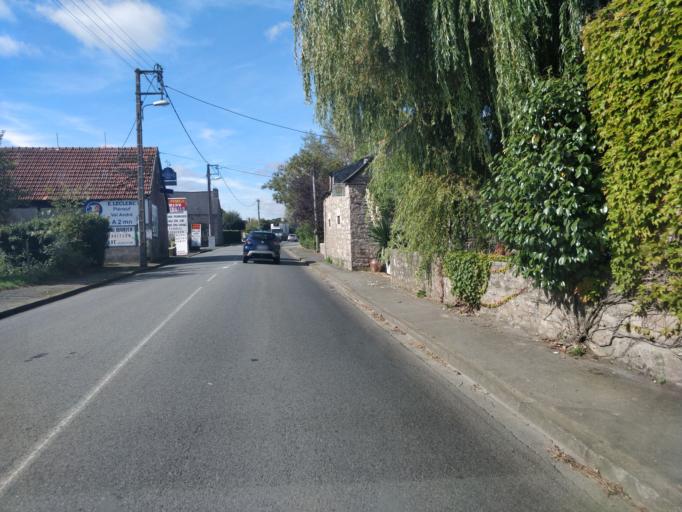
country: FR
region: Brittany
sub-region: Departement des Cotes-d'Armor
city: Erquy
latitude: 48.5977
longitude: -2.4741
